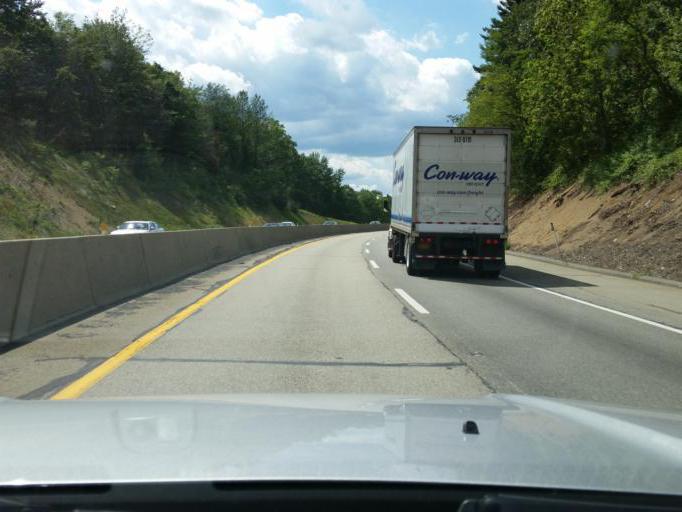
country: US
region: Pennsylvania
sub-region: Fulton County
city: McConnellsburg
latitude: 40.0431
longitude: -78.0292
